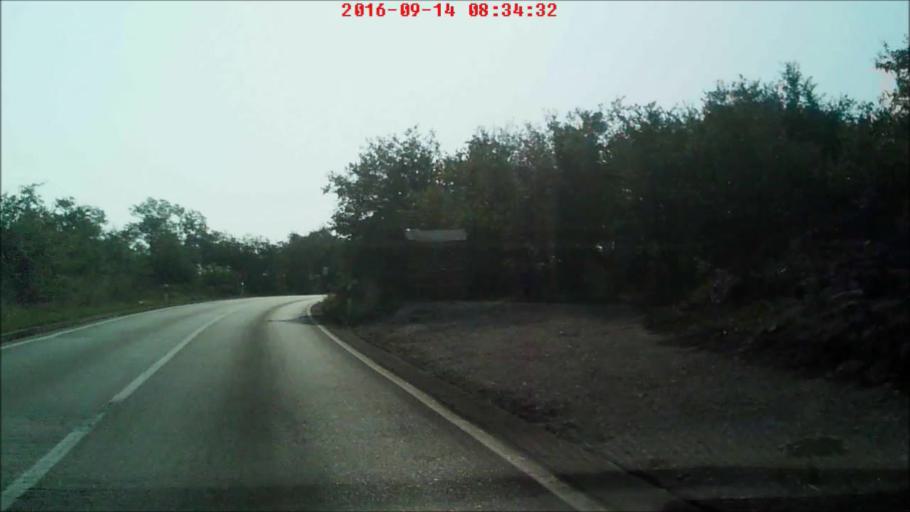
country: HR
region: Zadarska
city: Policnik
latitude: 44.1510
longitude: 15.3219
